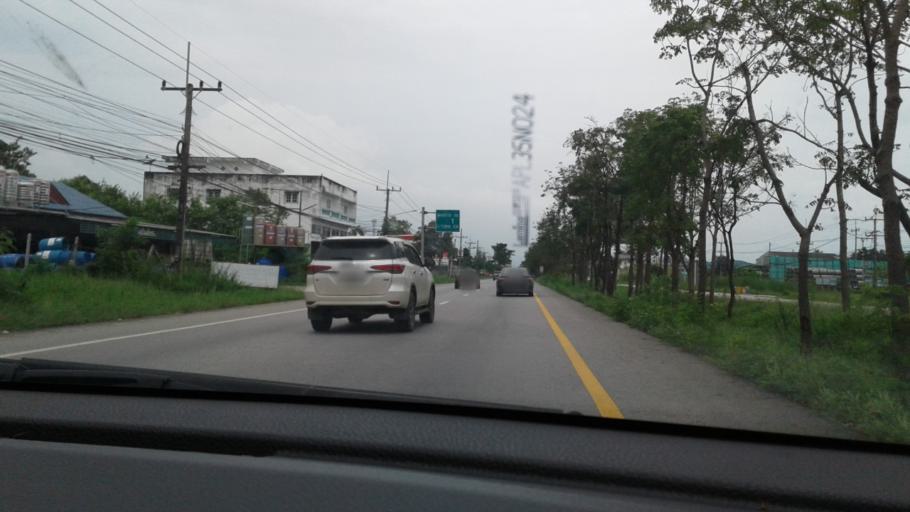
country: TH
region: Prachuap Khiri Khan
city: Prachuap Khiri Khan
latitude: 11.7999
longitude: 99.7761
